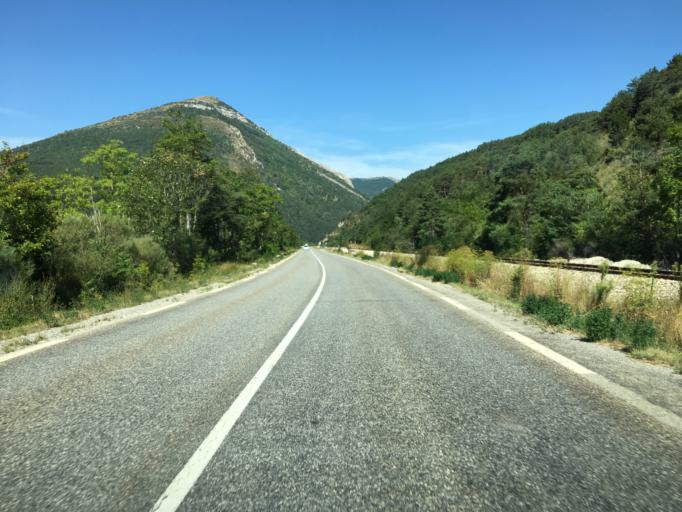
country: FR
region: Provence-Alpes-Cote d'Azur
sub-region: Departement des Hautes-Alpes
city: Veynes
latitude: 44.5721
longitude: 5.7334
